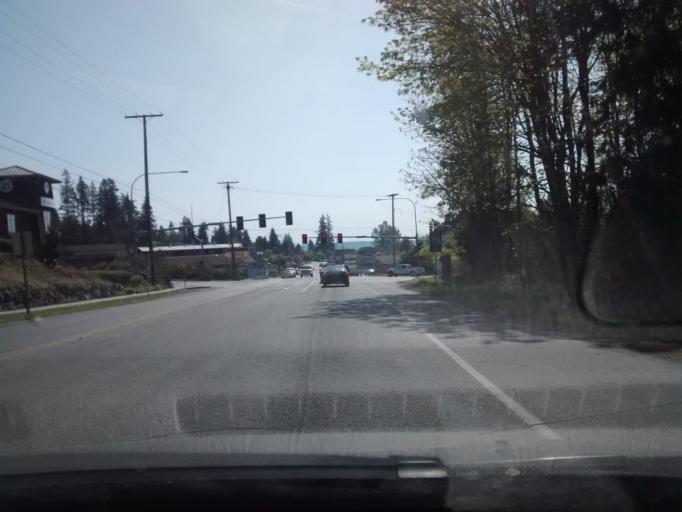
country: US
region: Washington
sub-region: Kitsap County
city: Kingston
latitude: 47.8033
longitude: -122.5052
